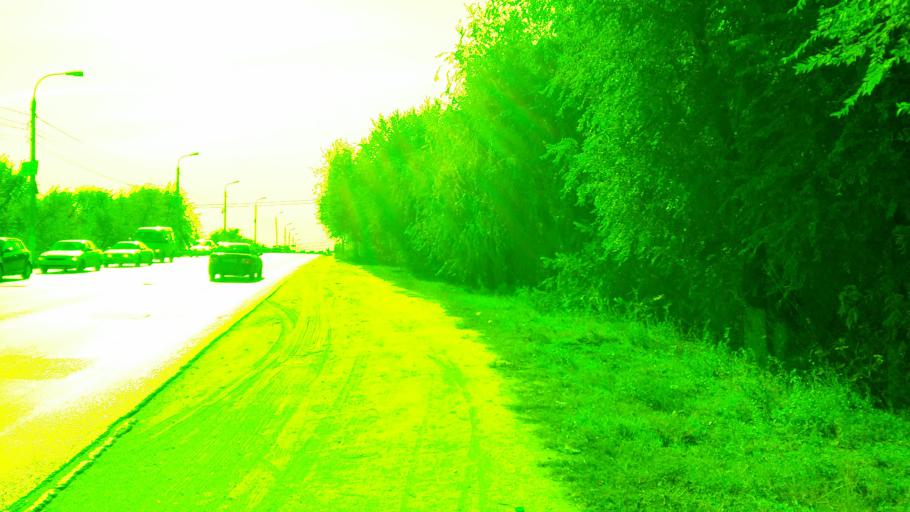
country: RU
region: Volgograd
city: Vodstroy
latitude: 48.8355
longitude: 44.6454
